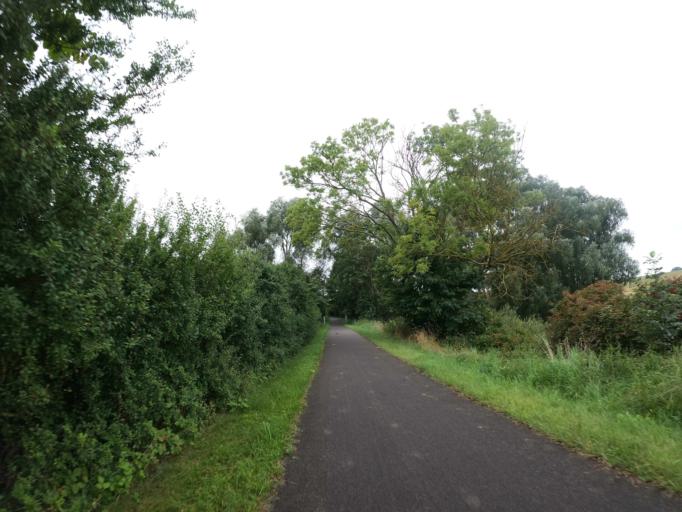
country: DE
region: Mecklenburg-Vorpommern
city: Poseritz
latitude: 54.2892
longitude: 13.2730
